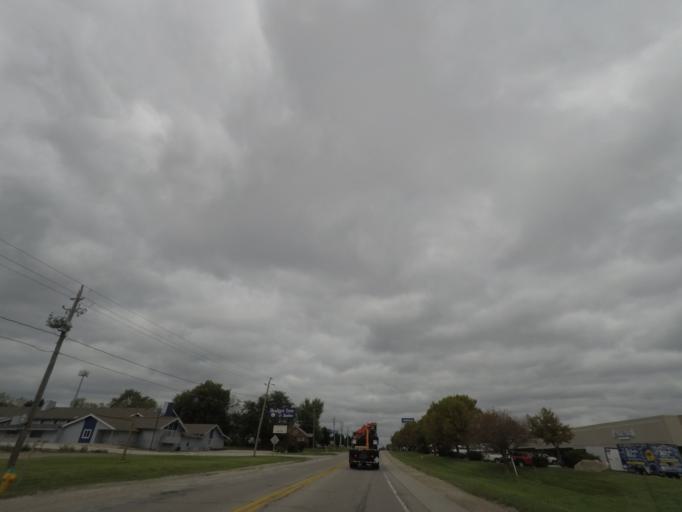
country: US
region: Iowa
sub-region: Polk County
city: Saylorville
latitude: 41.6547
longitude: -93.6005
